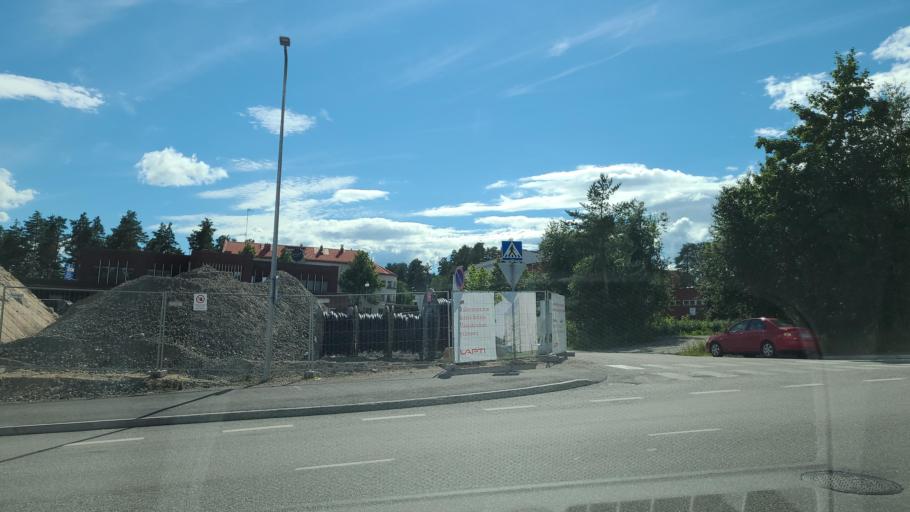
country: FI
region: Central Finland
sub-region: Jyvaeskylae
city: Saeynaetsalo
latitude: 62.2480
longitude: 25.8726
